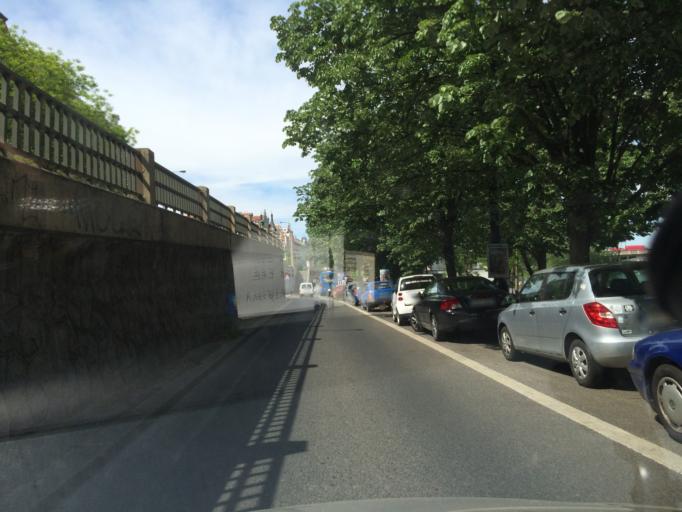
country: CZ
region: Praha
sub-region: Praha 2
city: Vysehrad
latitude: 50.0737
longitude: 14.4099
